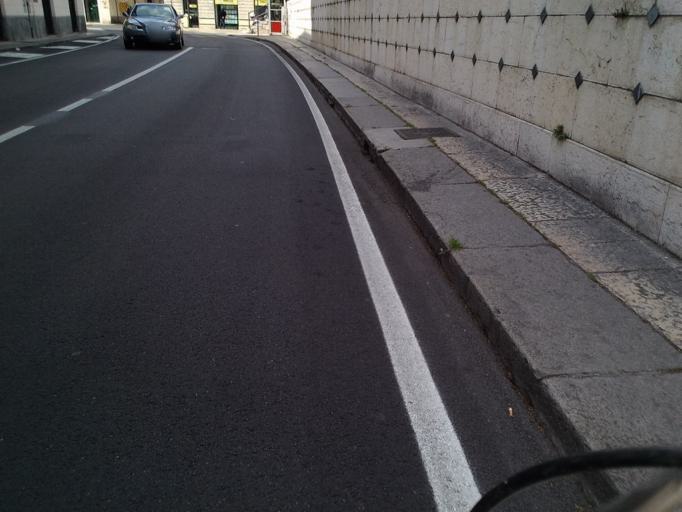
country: IT
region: Veneto
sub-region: Provincia di Verona
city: Verona
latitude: 45.4415
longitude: 10.9830
